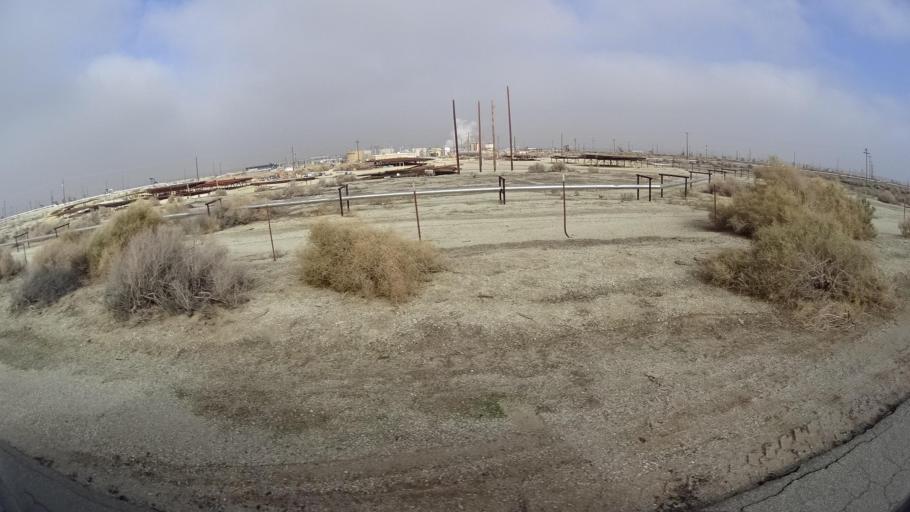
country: US
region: California
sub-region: Kern County
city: Maricopa
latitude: 35.0307
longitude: -119.3447
